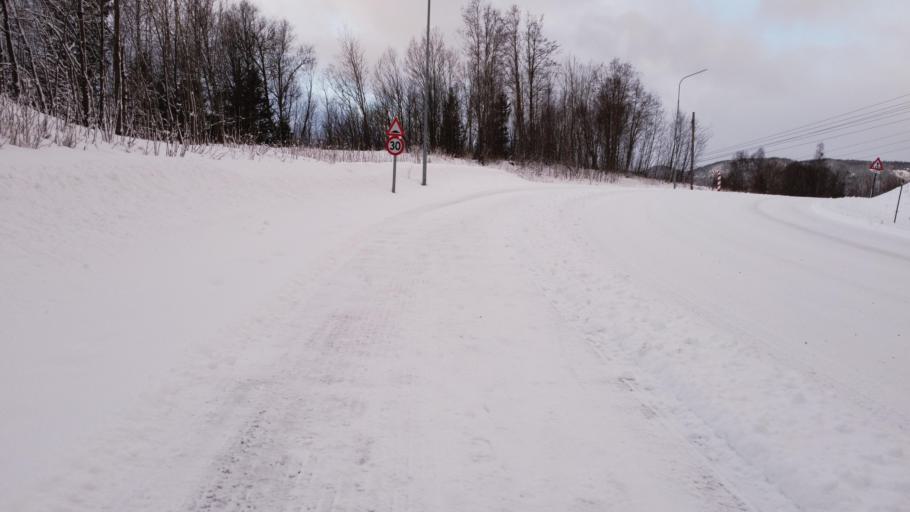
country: NO
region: Nordland
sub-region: Rana
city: Mo i Rana
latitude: 66.3268
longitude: 14.1574
